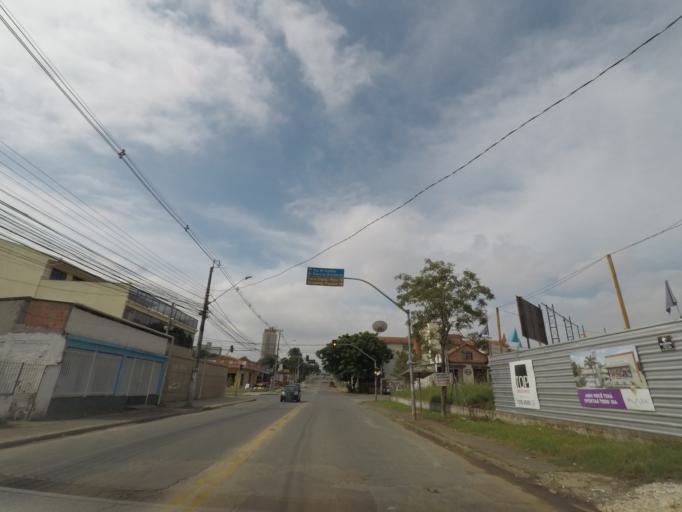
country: BR
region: Parana
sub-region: Curitiba
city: Curitiba
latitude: -25.4891
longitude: -49.3001
